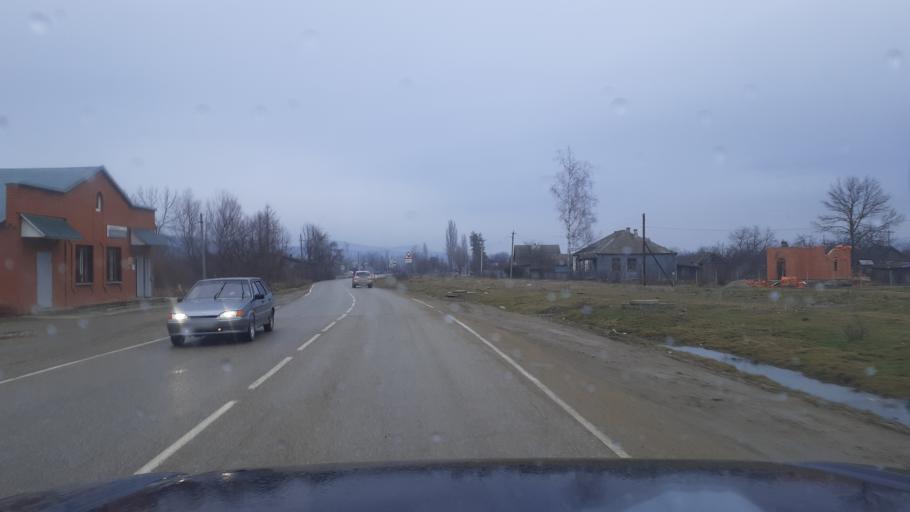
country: RU
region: Krasnodarskiy
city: Neftegorsk
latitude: 44.2481
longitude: 39.7659
